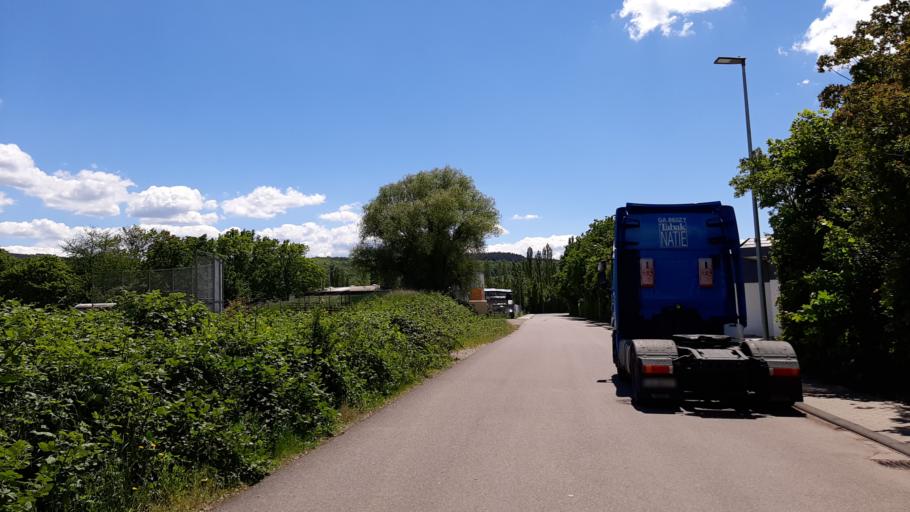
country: DE
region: Rheinland-Pfalz
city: Trier
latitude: 49.7310
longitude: 6.6152
